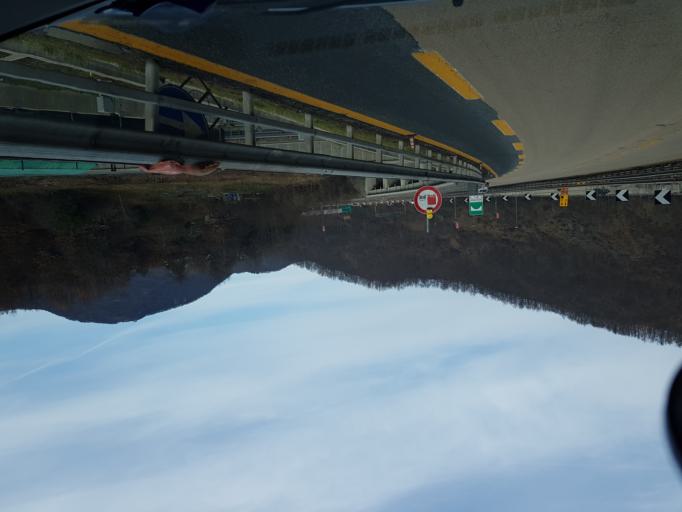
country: IT
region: Liguria
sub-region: Provincia di Genova
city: Ronco Scrivia
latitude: 44.6011
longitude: 8.9514
